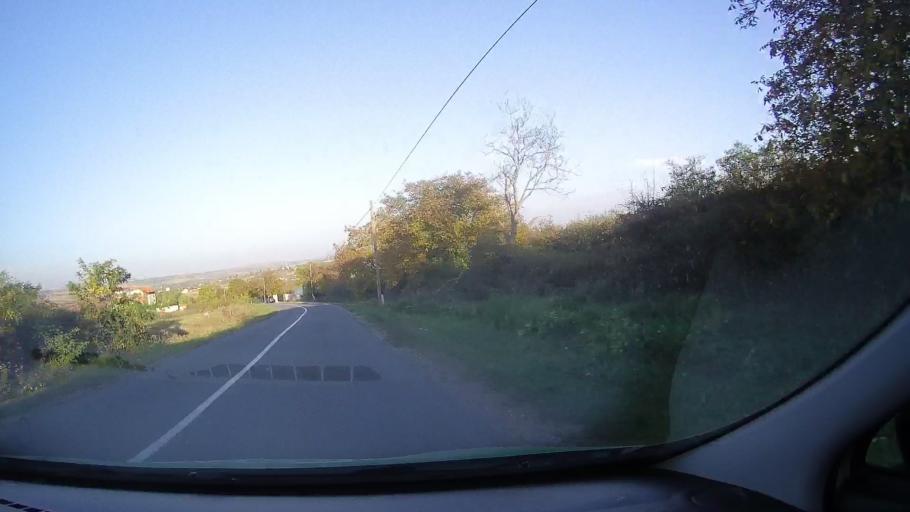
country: RO
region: Bihor
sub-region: Comuna Paleu
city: Paleu
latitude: 47.1094
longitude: 21.9320
